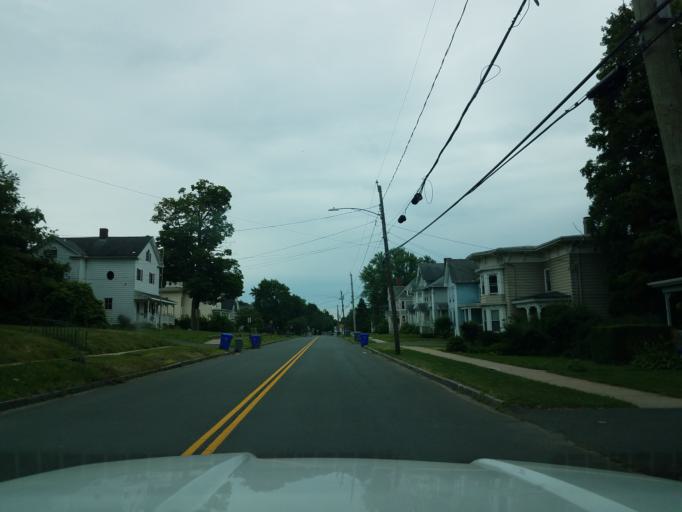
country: US
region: Connecticut
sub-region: Hartford County
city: Thompsonville
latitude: 41.9931
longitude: -72.5984
